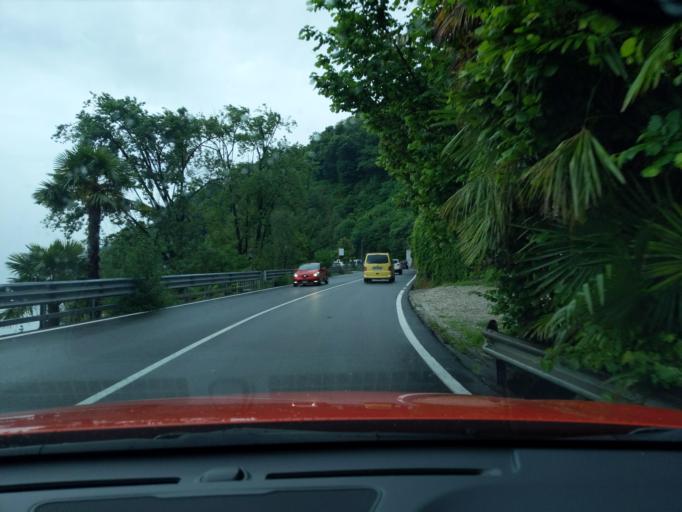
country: IT
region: Piedmont
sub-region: Provincia Verbano-Cusio-Ossola
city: Cannobio
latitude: 46.0874
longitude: 8.6914
